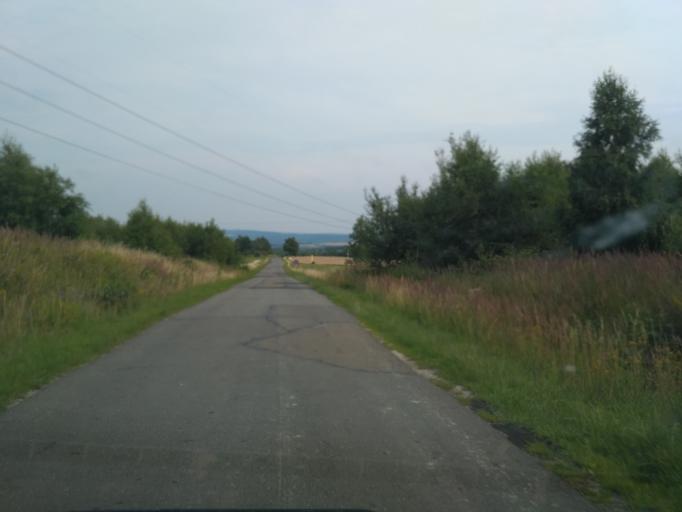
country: PL
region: Subcarpathian Voivodeship
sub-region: Powiat strzyzowski
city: Jawornik
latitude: 49.8686
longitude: 21.8611
